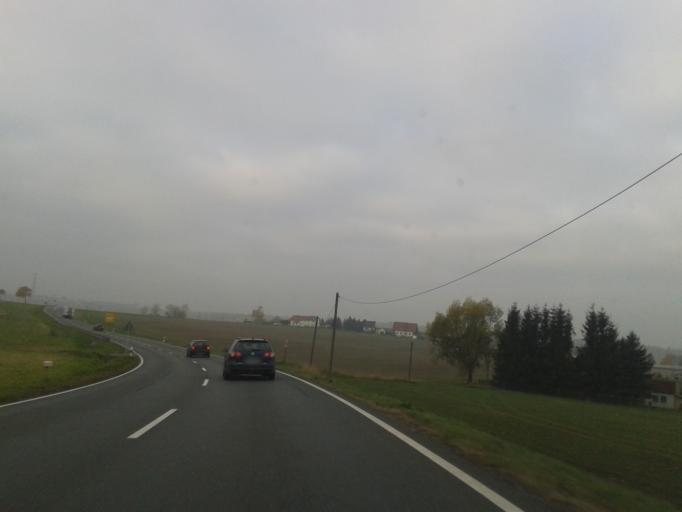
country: DE
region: Saxony
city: Niederschona
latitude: 50.9255
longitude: 13.3939
